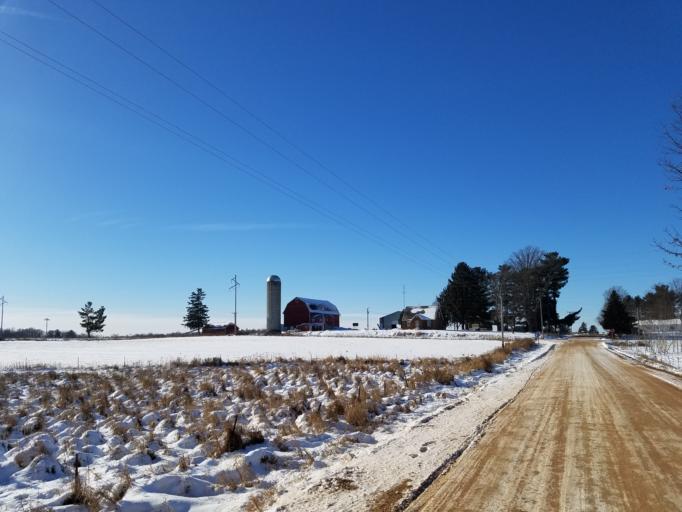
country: US
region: Wisconsin
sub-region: Clark County
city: Loyal
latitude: 44.5682
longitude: -90.3938
